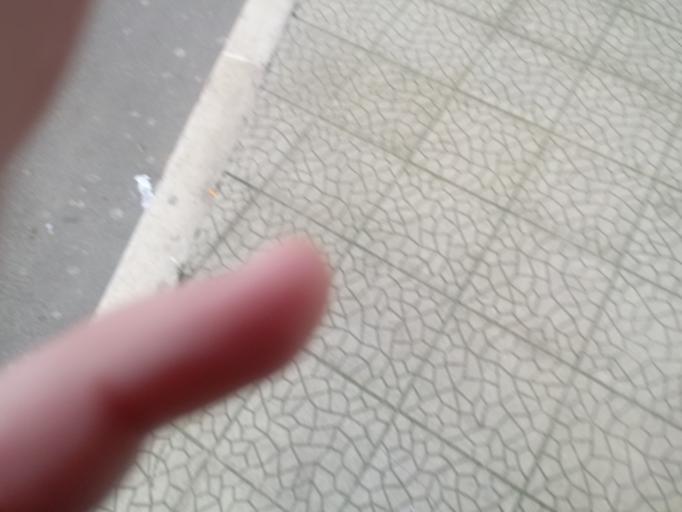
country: IT
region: Apulia
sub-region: Provincia di Barletta - Andria - Trani
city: Andria
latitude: 41.2174
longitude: 16.2959
